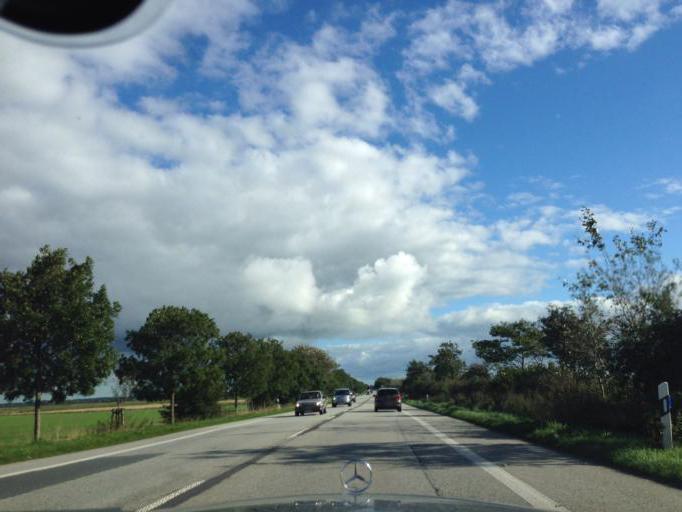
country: DE
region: Schleswig-Holstein
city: Risum-Lindholm
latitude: 54.7569
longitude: 8.8872
